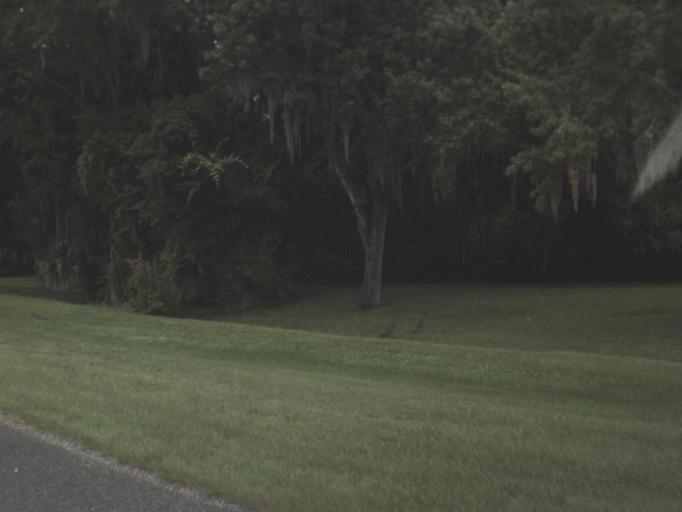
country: US
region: Florida
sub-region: Citrus County
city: Inverness
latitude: 28.8512
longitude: -82.2296
